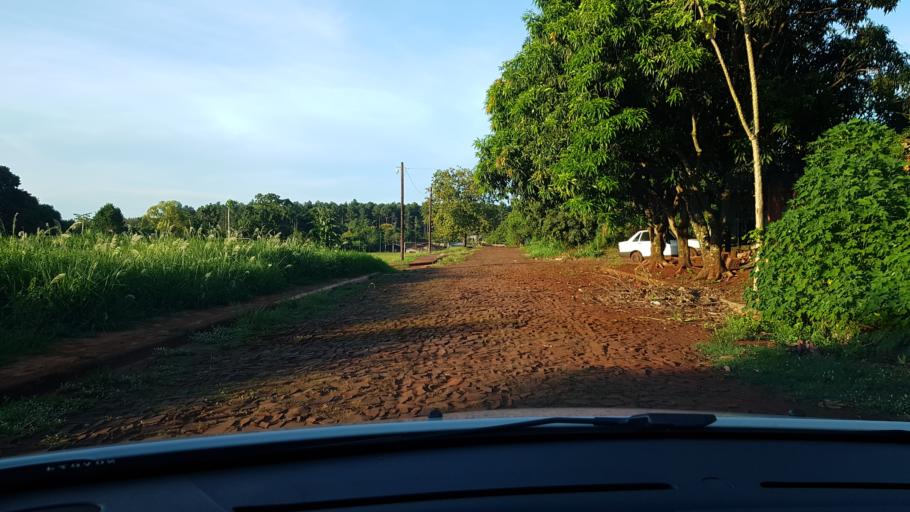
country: AR
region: Misiones
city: Puerto Libertad
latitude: -25.9173
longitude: -54.5824
